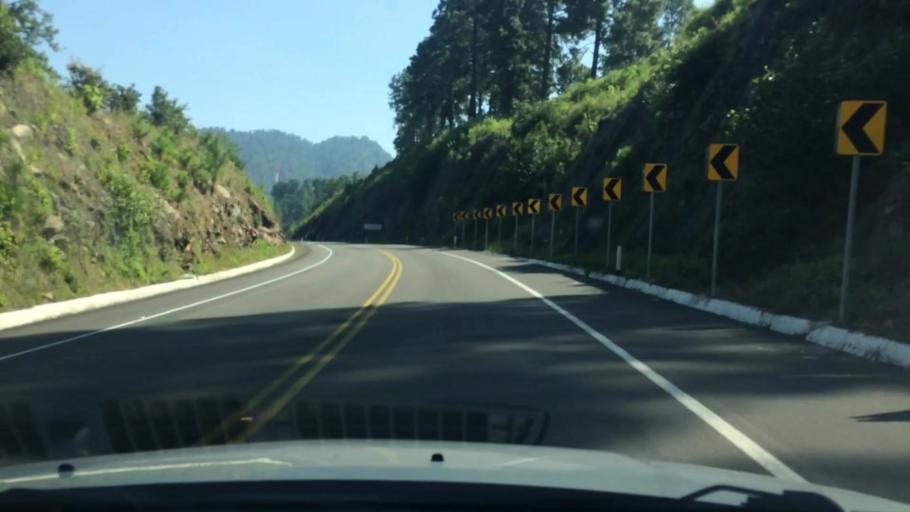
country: MX
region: Mexico
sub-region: Amanalco
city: Polvillos (San Bartolo Quinta Seccion)
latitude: 19.2207
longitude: -100.0875
